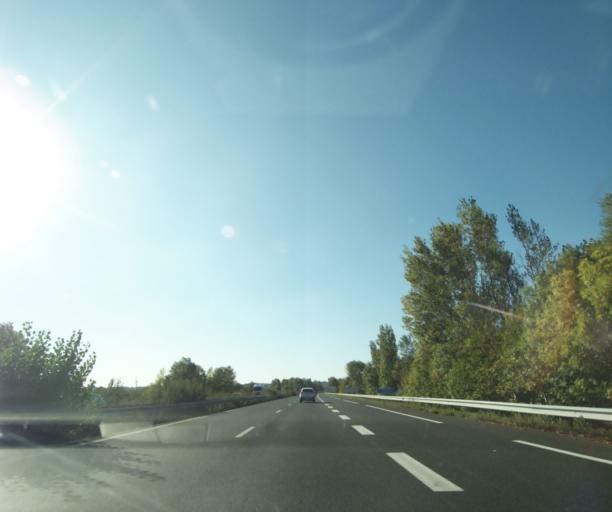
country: FR
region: Midi-Pyrenees
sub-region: Departement de la Haute-Garonne
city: Villefranche-de-Lauragais
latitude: 43.3917
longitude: 1.7110
